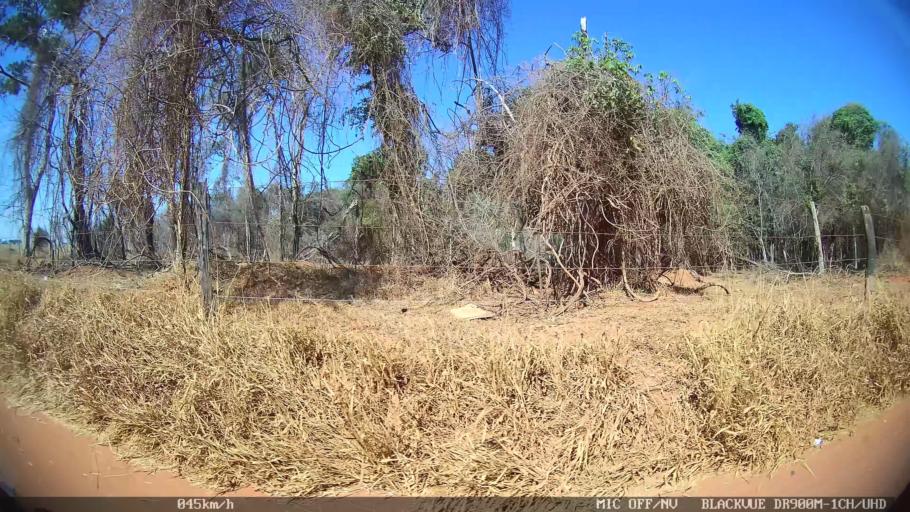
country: BR
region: Sao Paulo
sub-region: Sao Jose Do Rio Preto
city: Sao Jose do Rio Preto
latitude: -20.7423
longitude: -49.4285
